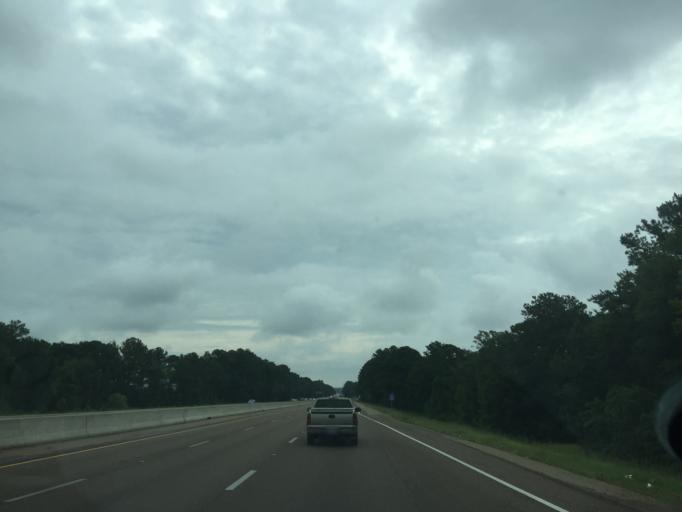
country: US
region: Mississippi
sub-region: Rankin County
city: Pearl
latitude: 32.2725
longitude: -90.0661
